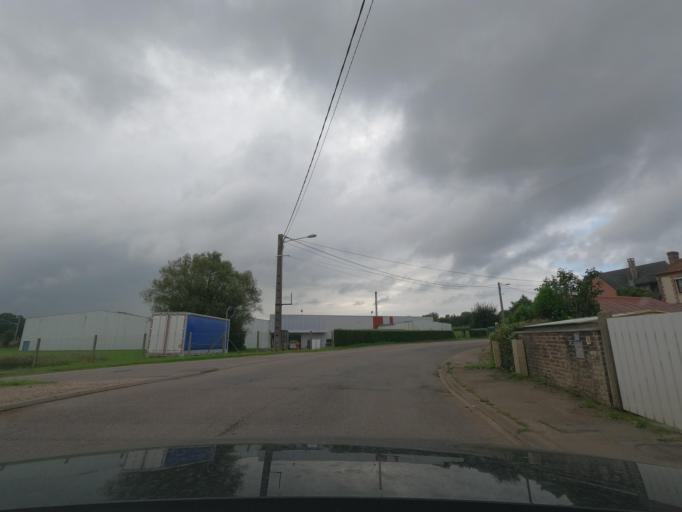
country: FR
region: Haute-Normandie
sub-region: Departement de la Seine-Maritime
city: Forges-les-Eaux
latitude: 49.6135
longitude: 1.5527
